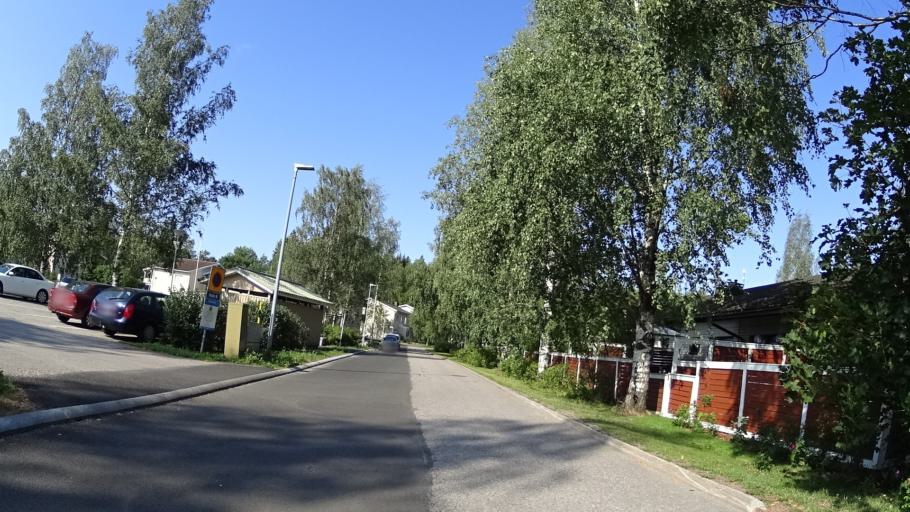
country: FI
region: Uusimaa
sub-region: Helsinki
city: Teekkarikylae
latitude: 60.2787
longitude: 24.8794
